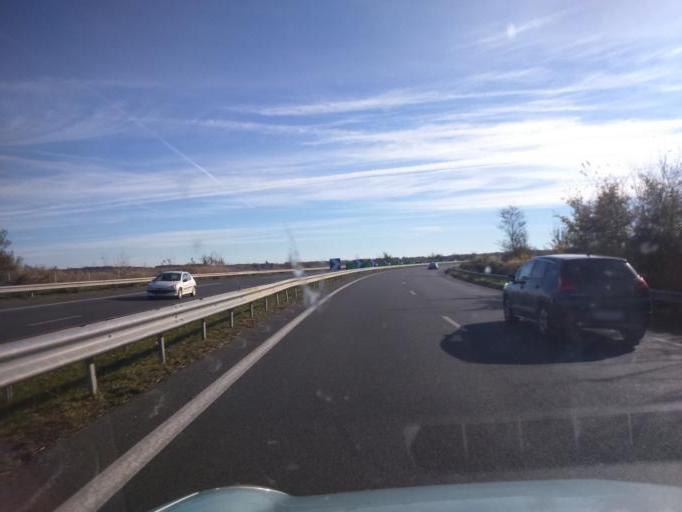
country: FR
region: Poitou-Charentes
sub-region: Departement de la Charente-Maritime
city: Saint-Laurent-de-la-Pree
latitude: 45.9802
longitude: -1.0010
